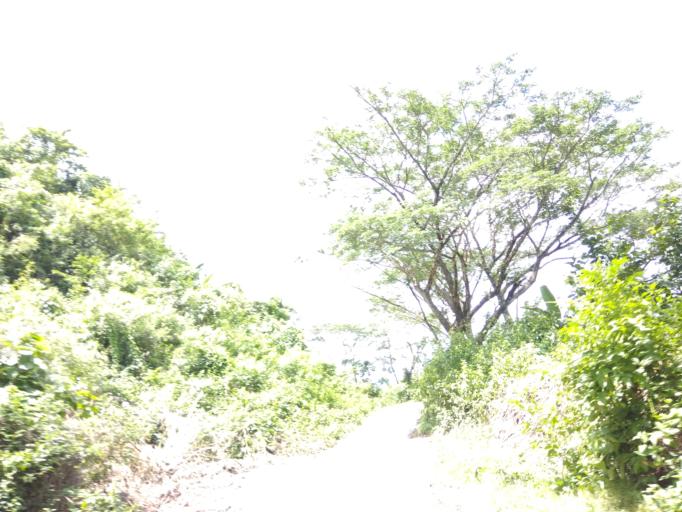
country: BD
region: Chittagong
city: Cox's Bazar
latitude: 21.6682
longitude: 92.3551
